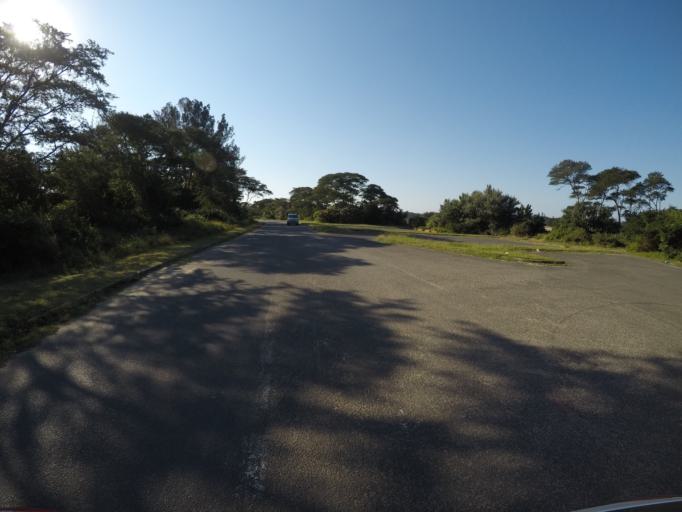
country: ZA
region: KwaZulu-Natal
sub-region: uThungulu District Municipality
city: Richards Bay
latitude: -28.7991
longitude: 32.0822
